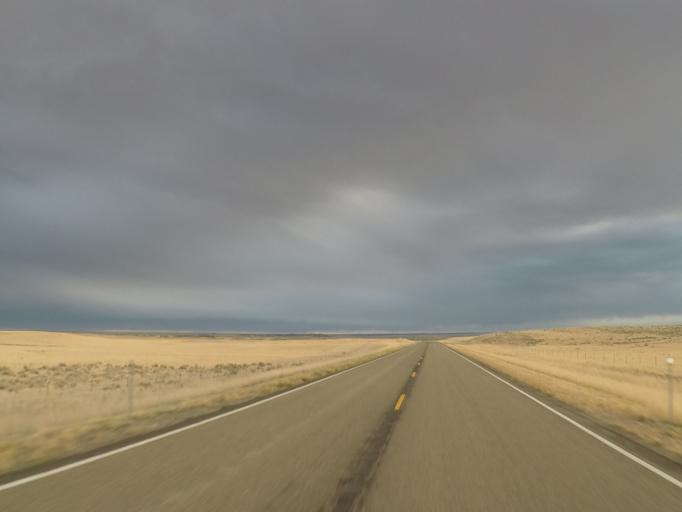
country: US
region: Montana
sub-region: Golden Valley County
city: Ryegate
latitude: 46.3924
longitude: -109.2575
